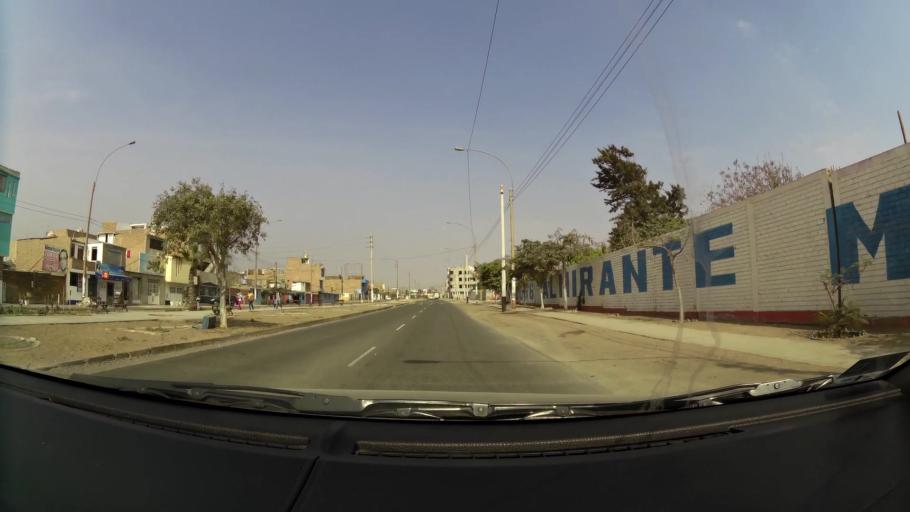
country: PE
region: Lima
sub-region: Lima
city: Santa Rosa
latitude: -11.7829
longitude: -77.1594
